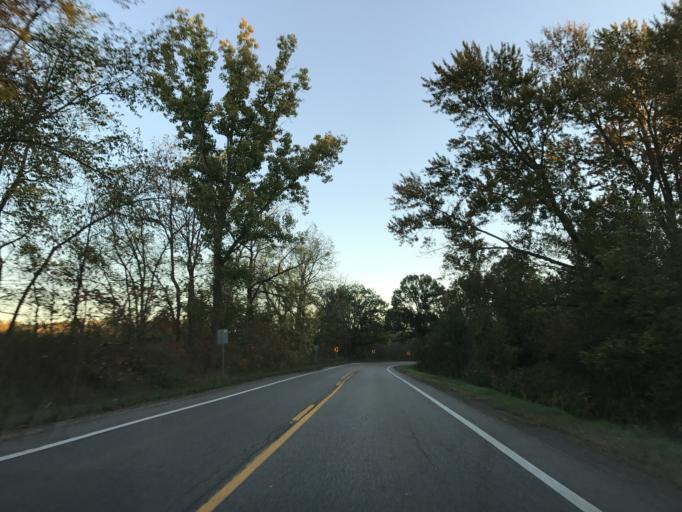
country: US
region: Michigan
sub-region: Oakland County
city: South Lyon
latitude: 42.4834
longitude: -83.6127
